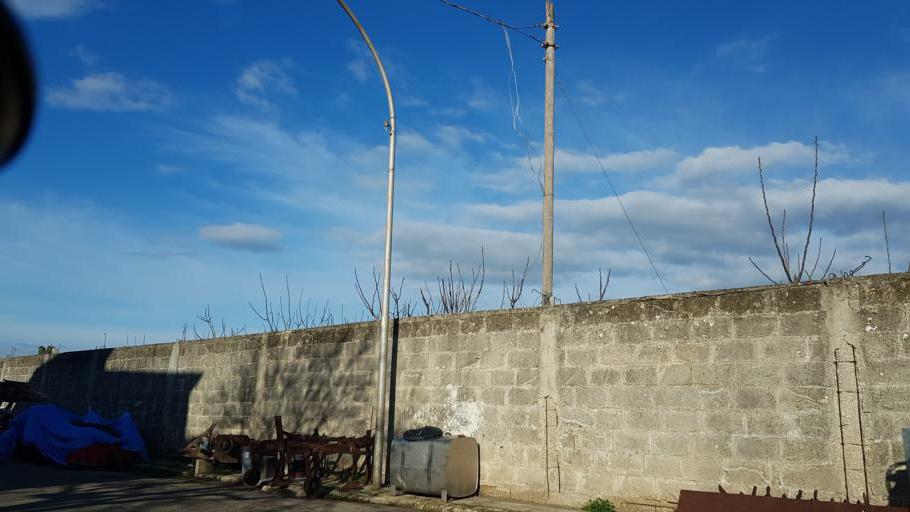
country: IT
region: Apulia
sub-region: Provincia di Brindisi
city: La Rosa
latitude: 40.6103
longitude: 17.9521
